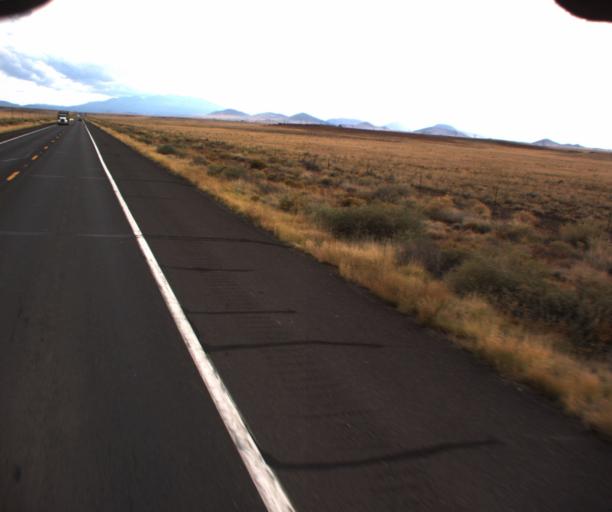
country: US
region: Arizona
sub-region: Coconino County
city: Flagstaff
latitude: 35.6806
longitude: -111.5074
